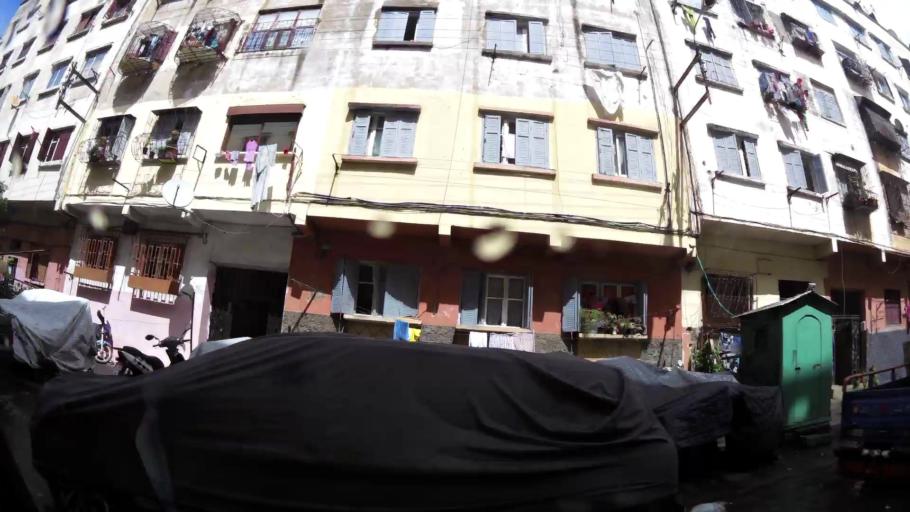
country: MA
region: Grand Casablanca
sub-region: Casablanca
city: Casablanca
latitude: 33.5449
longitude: -7.5634
